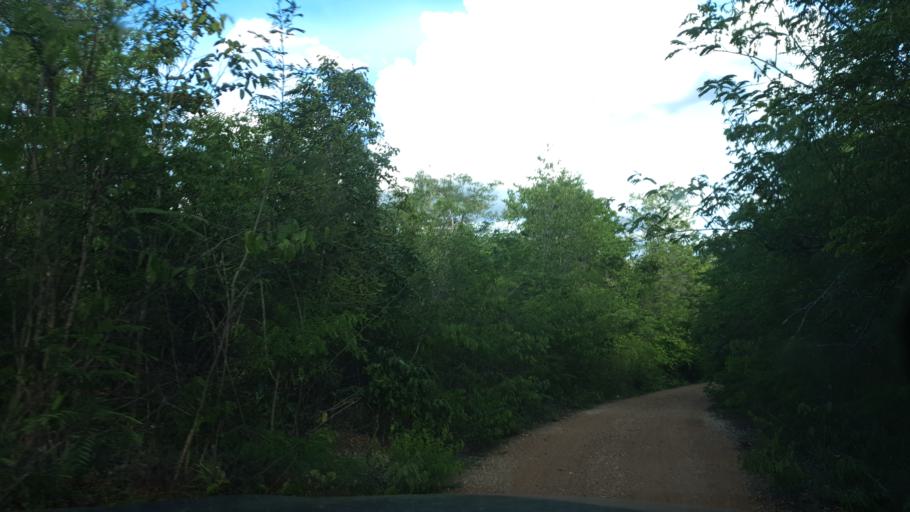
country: TH
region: Lampang
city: Sop Prap
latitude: 17.8864
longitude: 99.2911
